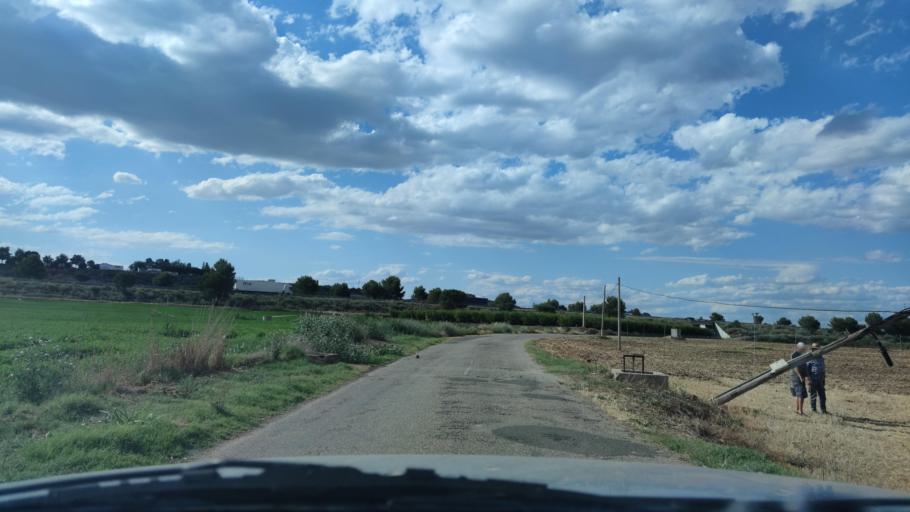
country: ES
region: Catalonia
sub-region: Provincia de Lleida
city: Alcarras
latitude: 41.5998
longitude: 0.5286
